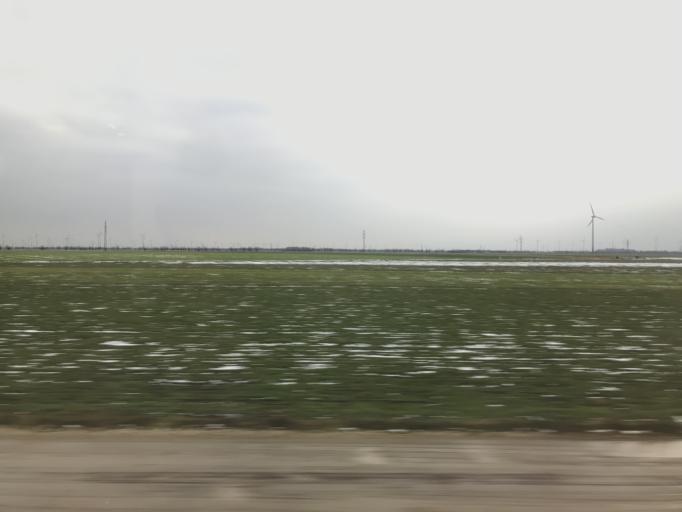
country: AT
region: Burgenland
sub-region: Politischer Bezirk Neusiedl am See
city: Potzneusiedl
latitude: 47.9895
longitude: 16.9314
